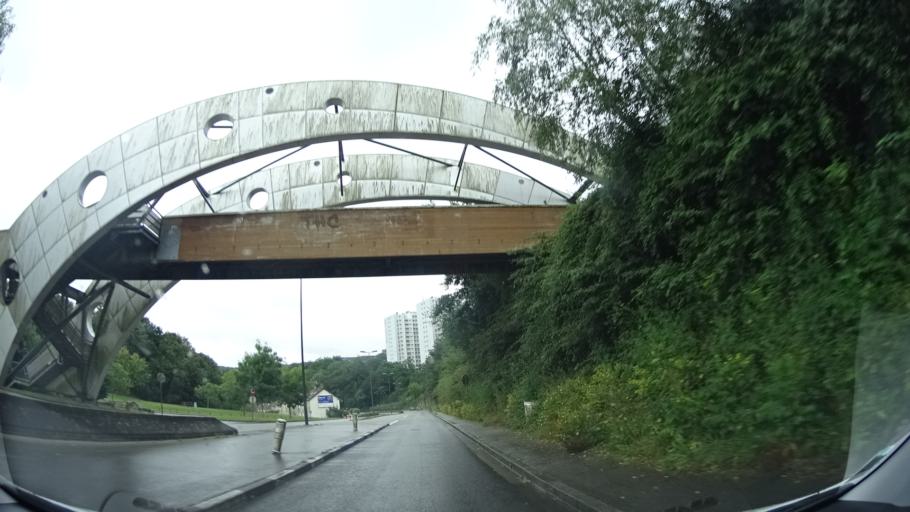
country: FR
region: Lower Normandy
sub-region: Departement de la Manche
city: Octeville
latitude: 49.6296
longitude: -1.6300
